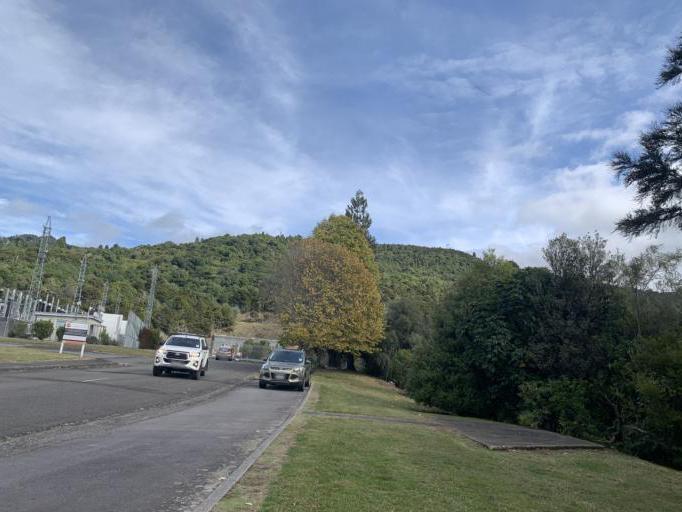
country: NZ
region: Waikato
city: Turangi
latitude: -38.9807
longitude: 175.7711
